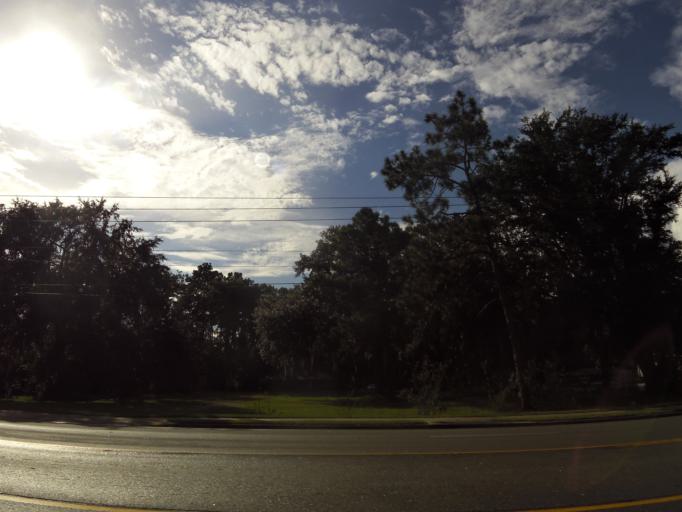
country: US
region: Georgia
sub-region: Liberty County
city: Walthourville
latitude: 31.7977
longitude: -81.6063
